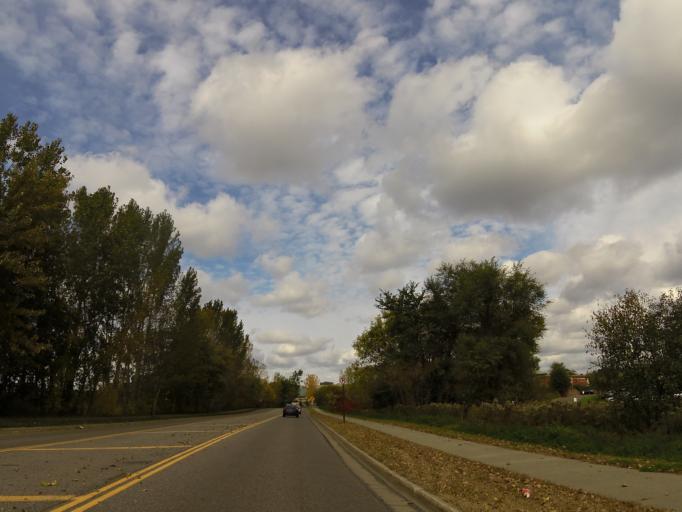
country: US
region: Minnesota
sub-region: Hennepin County
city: Eden Prairie
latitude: 44.8526
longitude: -93.4371
